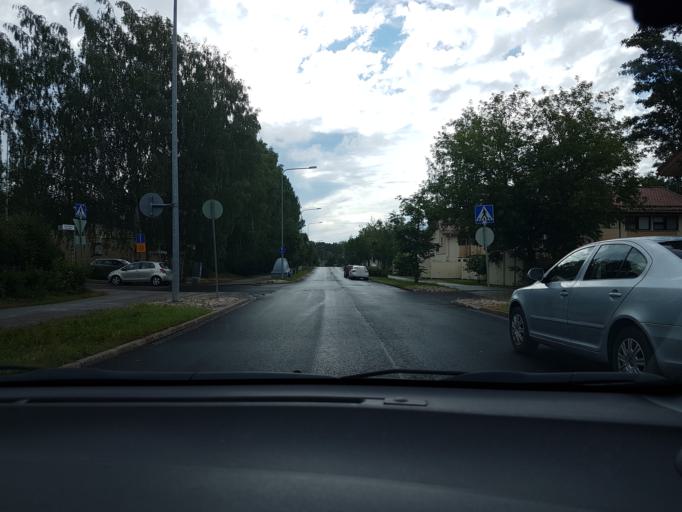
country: FI
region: Uusimaa
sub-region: Helsinki
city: Vantaa
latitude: 60.2204
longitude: 25.1124
